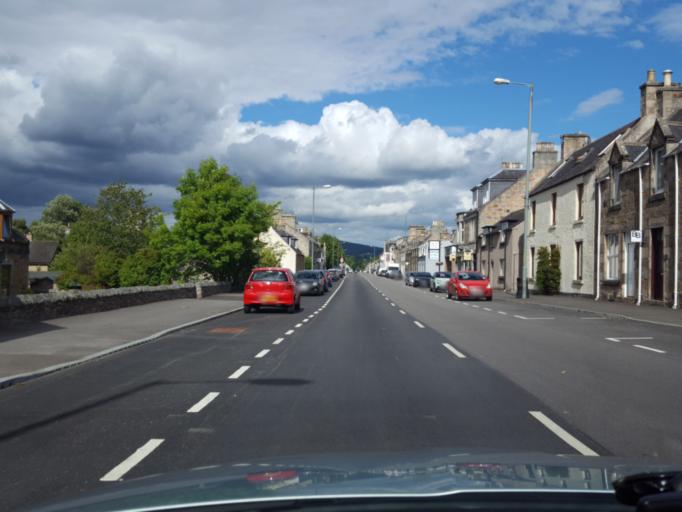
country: GB
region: Scotland
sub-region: Moray
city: Rothes
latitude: 57.4694
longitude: -3.2277
